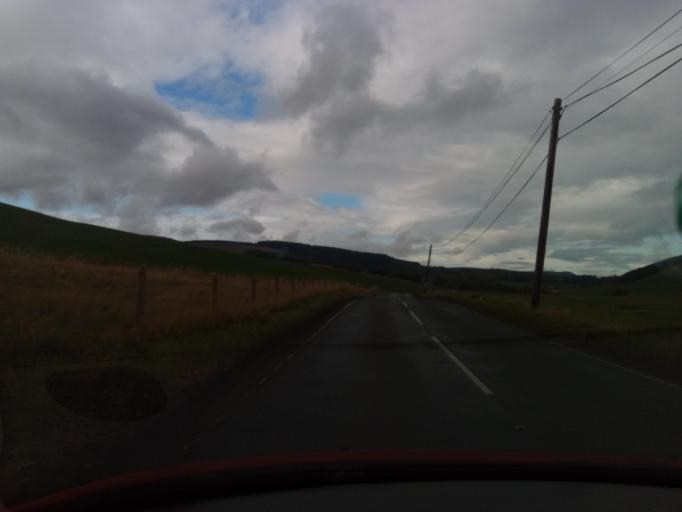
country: GB
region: Scotland
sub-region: The Scottish Borders
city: West Linton
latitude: 55.6722
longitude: -3.3323
